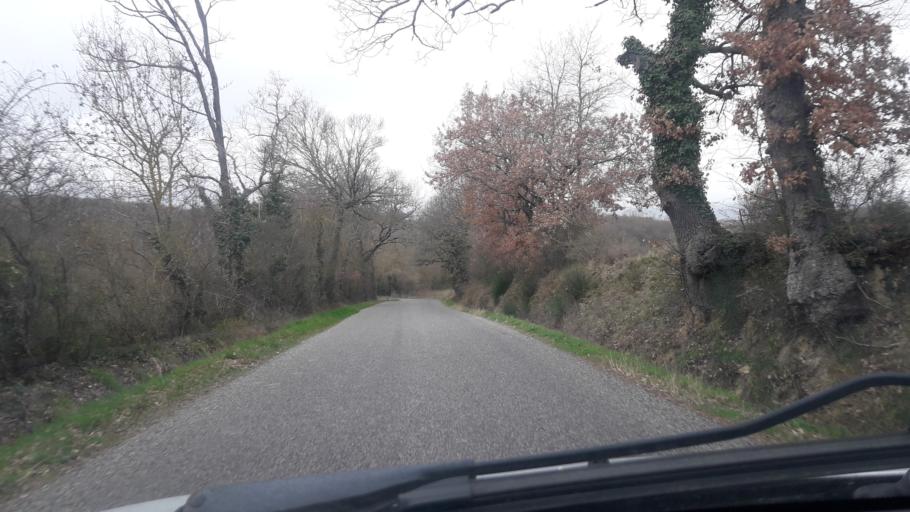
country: FR
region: Midi-Pyrenees
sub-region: Departement du Gers
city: Gimont
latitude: 43.6554
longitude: 0.9788
